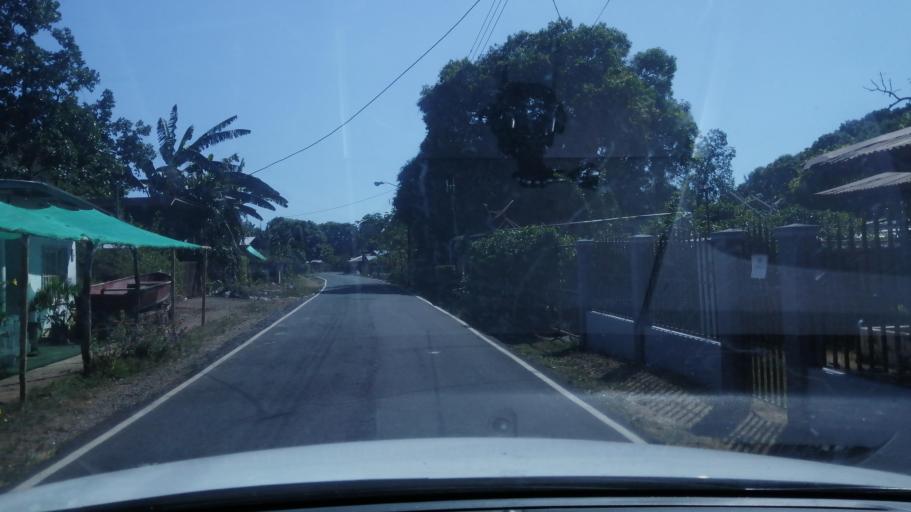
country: PA
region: Chiriqui
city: San Felix
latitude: 8.2933
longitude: -81.8697
